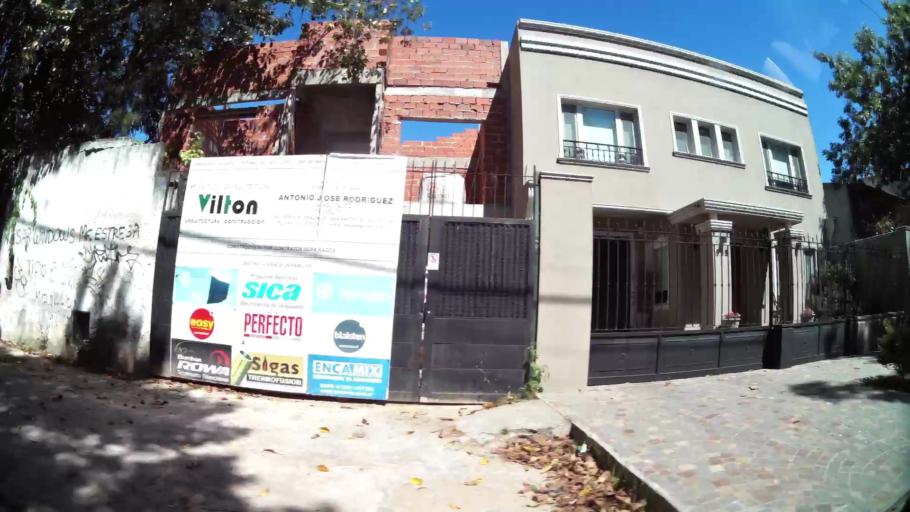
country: AR
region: Buenos Aires
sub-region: Partido de San Isidro
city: San Isidro
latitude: -34.4647
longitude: -58.5052
